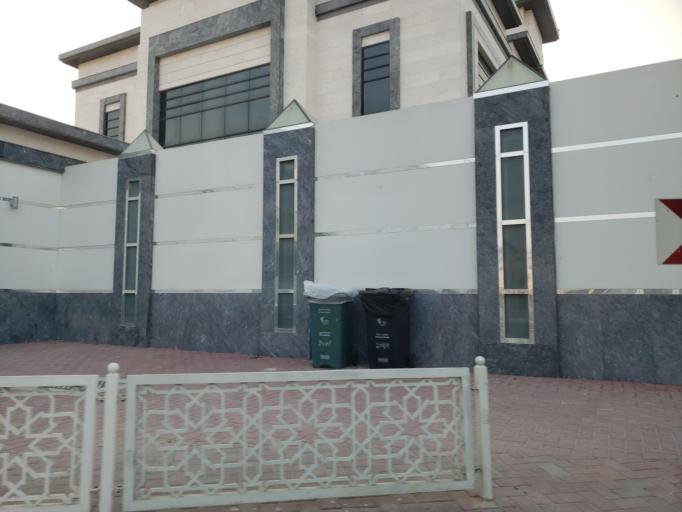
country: AE
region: Dubai
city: Dubai
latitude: 25.1917
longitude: 55.2301
